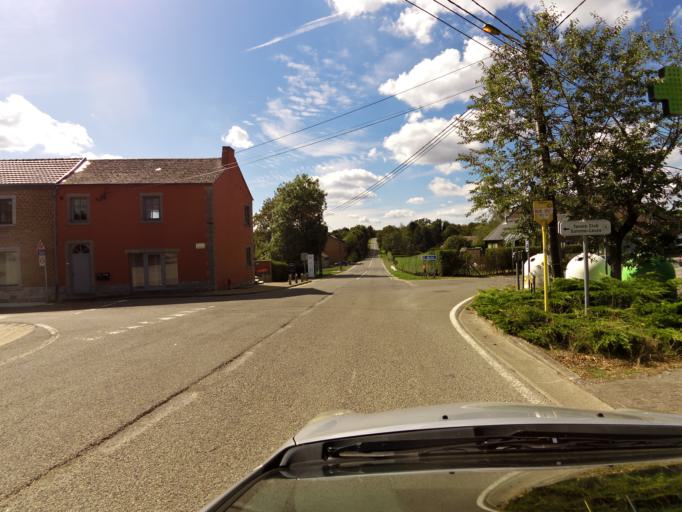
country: BE
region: Wallonia
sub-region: Province de Namur
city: Somme-Leuze
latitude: 50.3369
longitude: 5.3670
